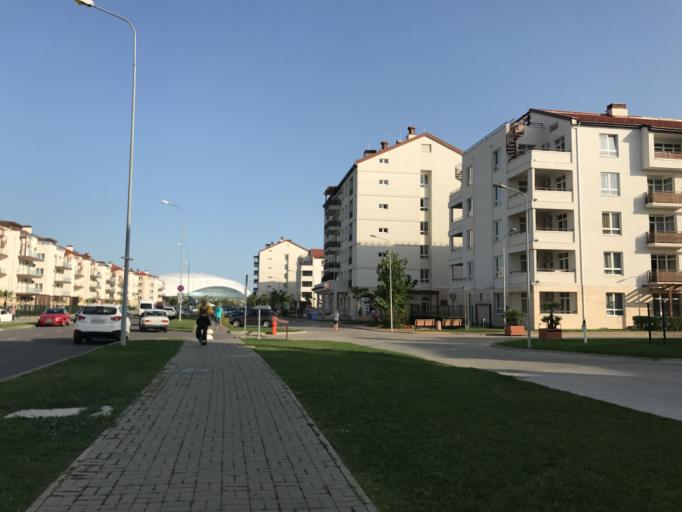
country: RU
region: Krasnodarskiy
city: Adler
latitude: 43.4080
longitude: 39.9407
